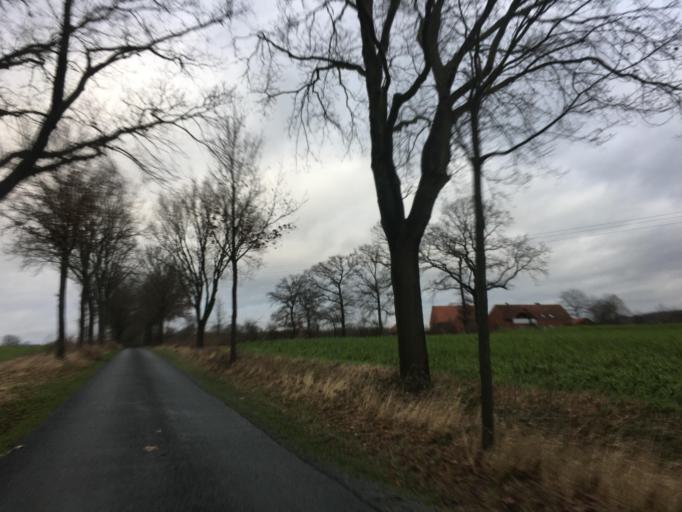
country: DE
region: North Rhine-Westphalia
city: Olfen
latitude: 51.7630
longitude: 7.3548
